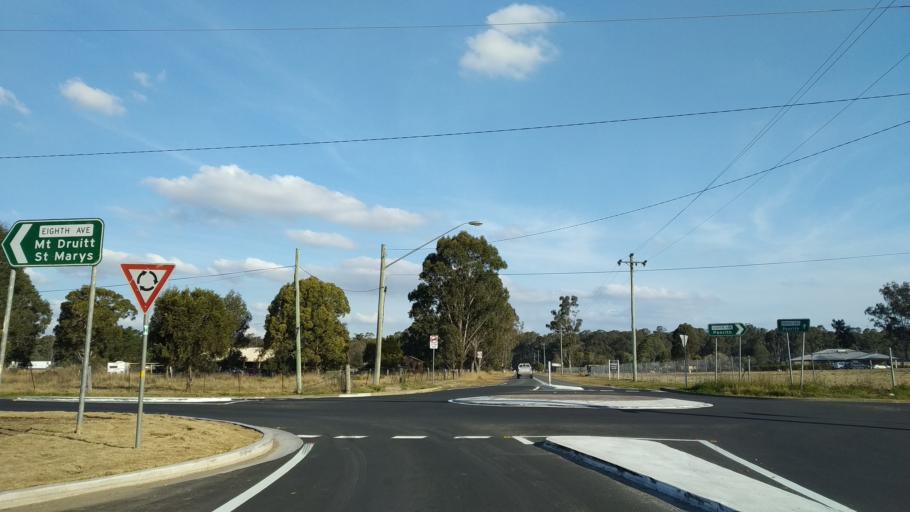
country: AU
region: New South Wales
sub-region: Penrith Municipality
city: Werrington County
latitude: -33.7125
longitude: 150.7561
